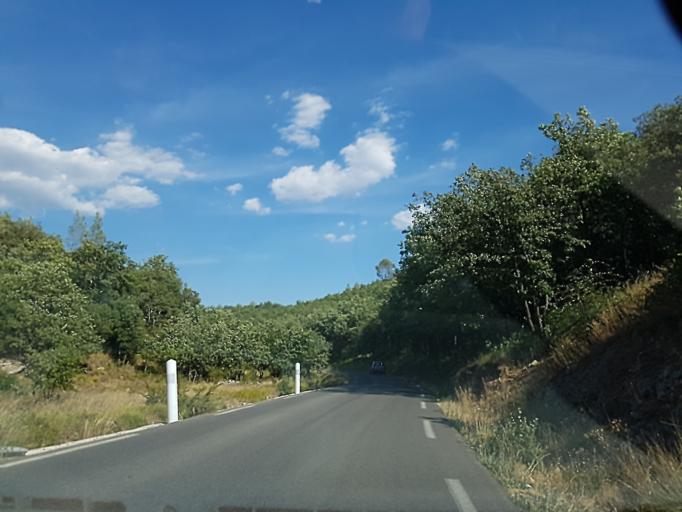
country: FR
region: Provence-Alpes-Cote d'Azur
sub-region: Departement du Var
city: Bras
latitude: 43.4601
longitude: 5.9106
